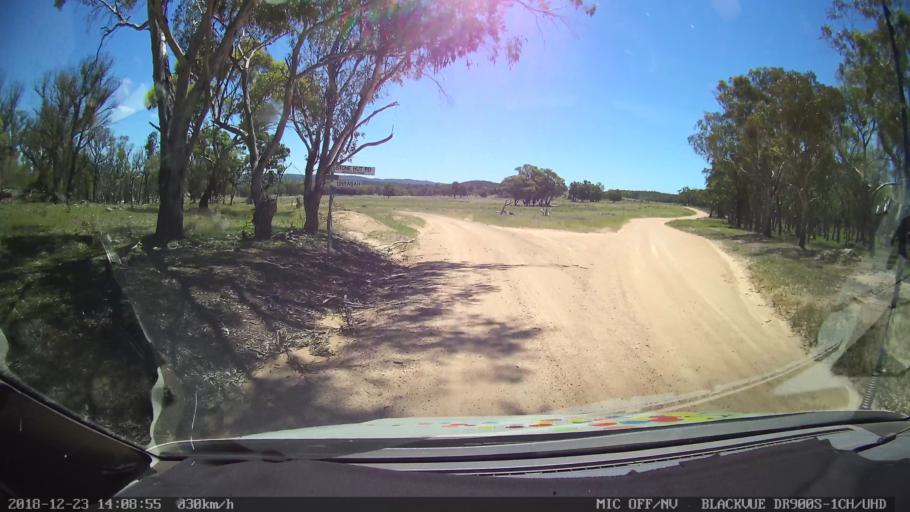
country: AU
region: New South Wales
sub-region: Tamworth Municipality
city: Manilla
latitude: -30.6429
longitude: 151.0653
